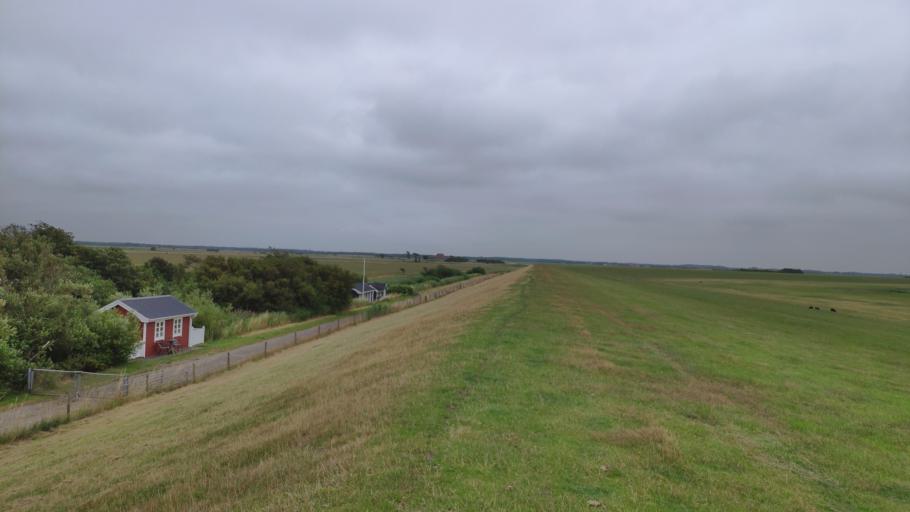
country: DK
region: South Denmark
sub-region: Esbjerg Kommune
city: Ribe
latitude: 55.3346
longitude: 8.6794
